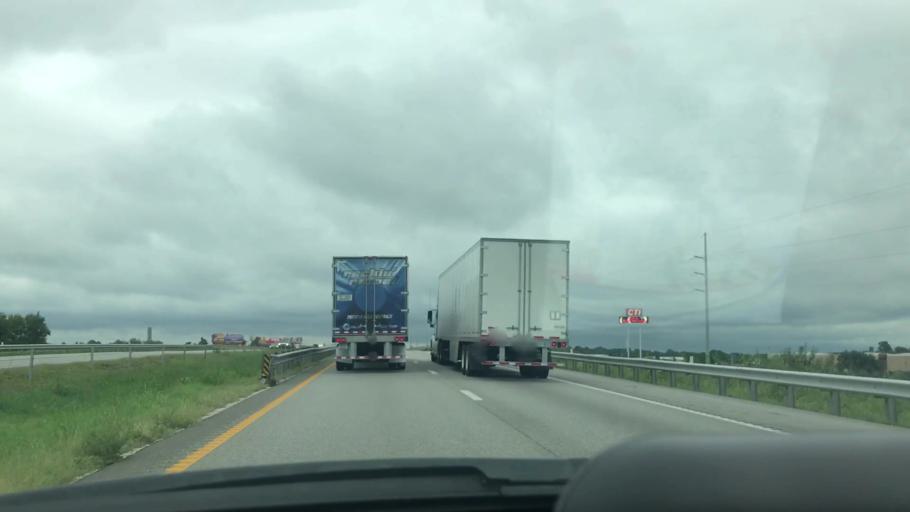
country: US
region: Missouri
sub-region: Greene County
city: Springfield
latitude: 37.2195
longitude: -93.3775
